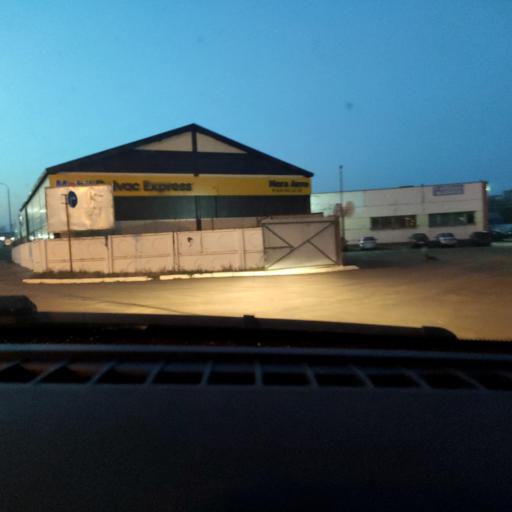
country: RU
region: Voronezj
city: Somovo
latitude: 51.6764
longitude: 39.3000
